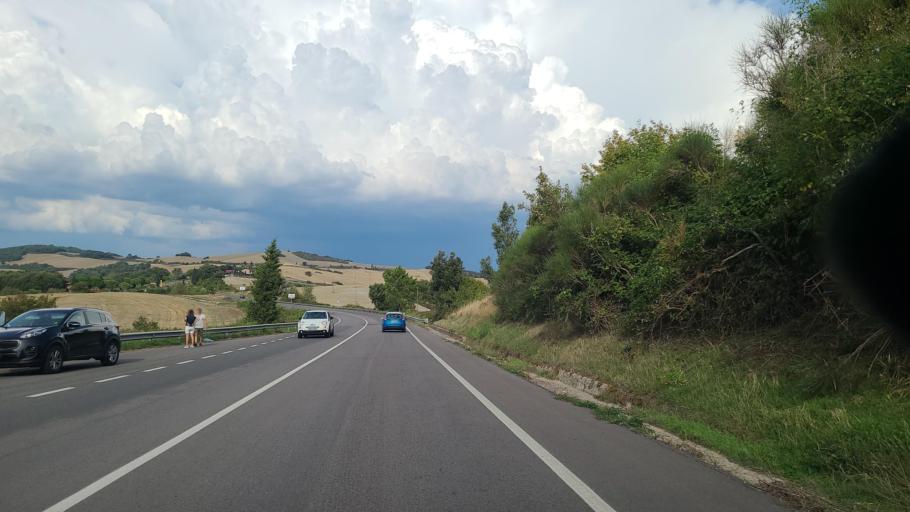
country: IT
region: Tuscany
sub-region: Province of Pisa
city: Volterra
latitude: 43.3954
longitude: 10.9581
